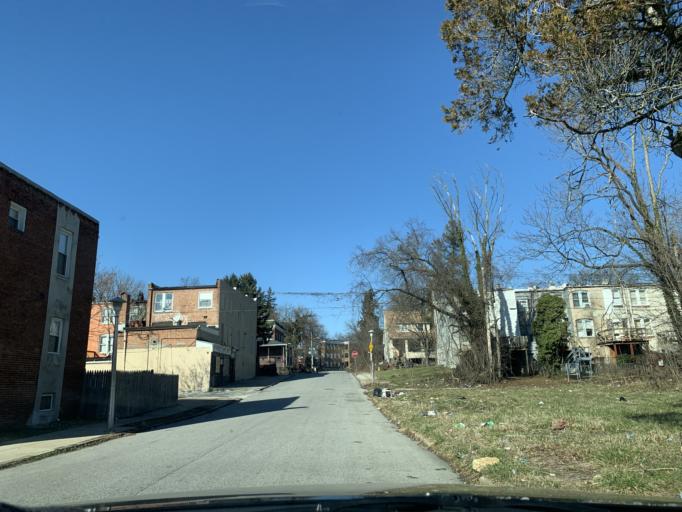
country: US
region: Maryland
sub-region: Baltimore County
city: Lochearn
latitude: 39.3230
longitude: -76.6863
